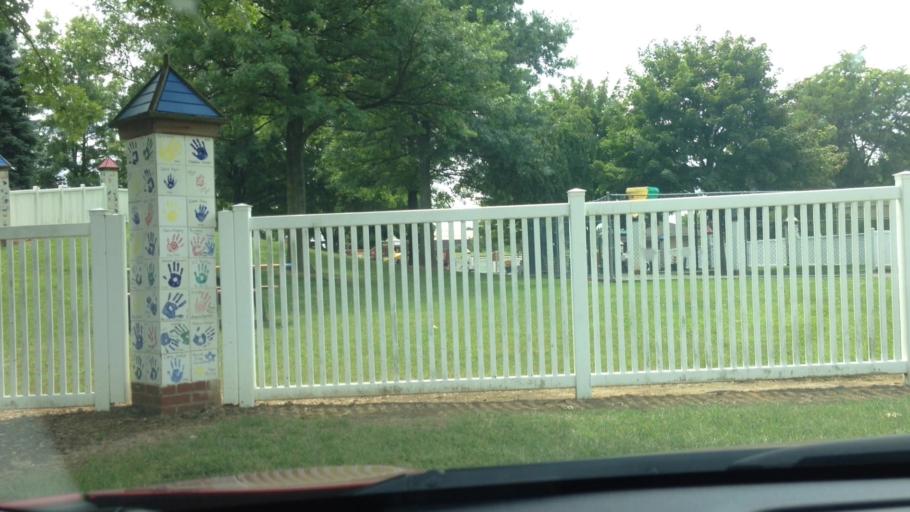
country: US
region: Ohio
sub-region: Stark County
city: Perry Heights
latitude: 40.8632
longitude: -81.4924
